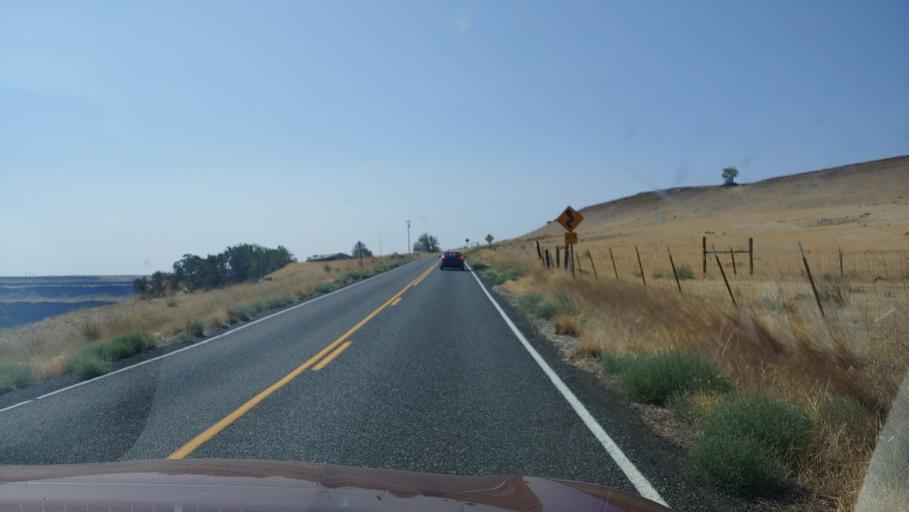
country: US
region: Washington
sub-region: Klickitat County
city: Goldendale
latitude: 45.6980
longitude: -120.8042
